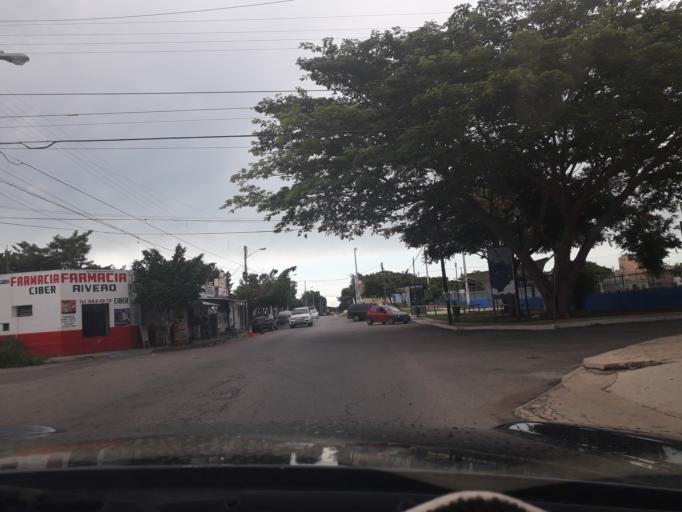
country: MX
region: Yucatan
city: Merida
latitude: 20.9413
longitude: -89.6397
